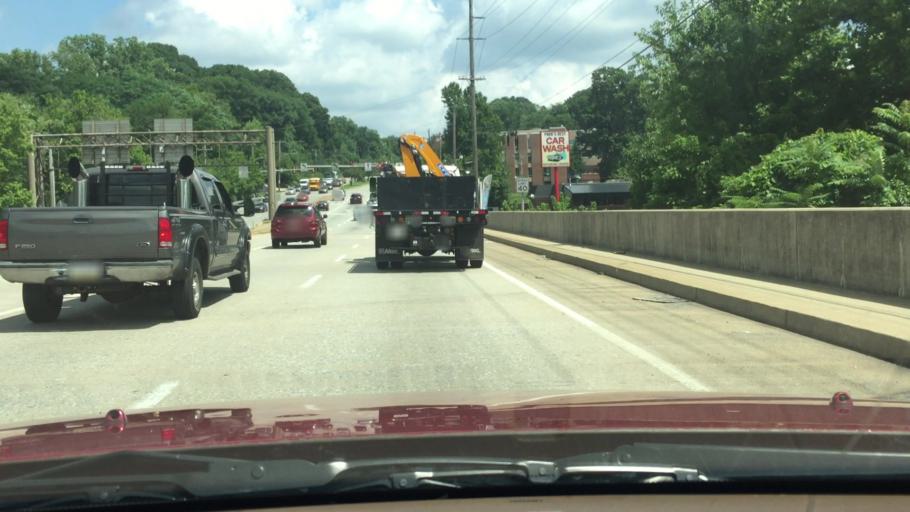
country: US
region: Pennsylvania
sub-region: Delaware County
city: Broomall
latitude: 39.9773
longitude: -75.3367
